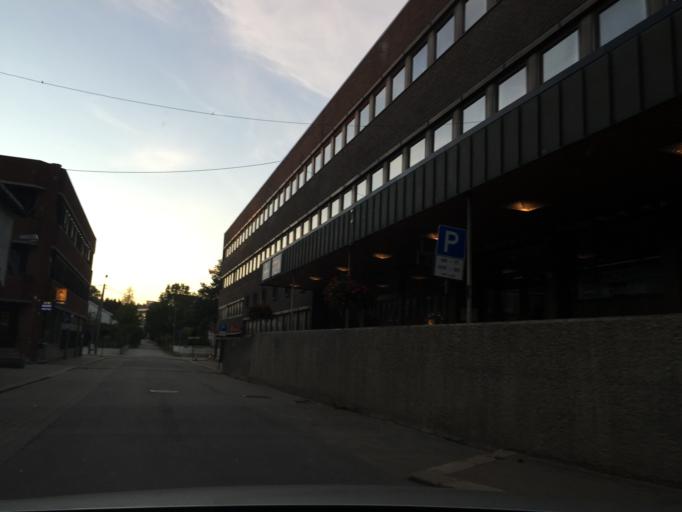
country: NO
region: Hedmark
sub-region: Kongsvinger
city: Kongsvinger
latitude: 60.1913
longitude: 11.9982
